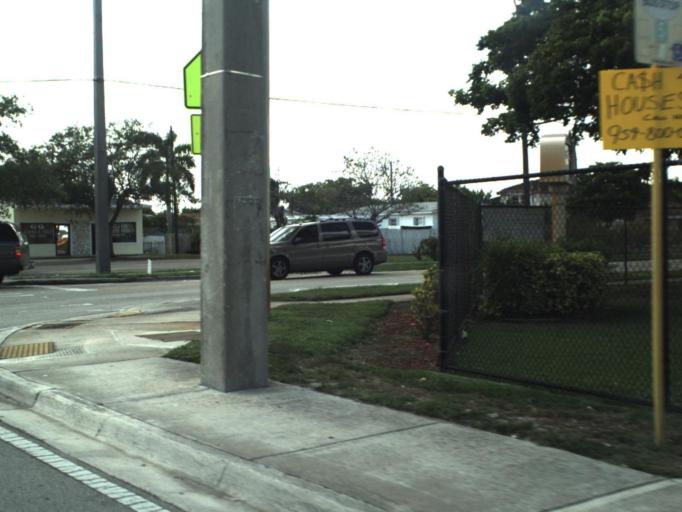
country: US
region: Florida
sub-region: Broward County
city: Carver Ranches
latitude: 25.9954
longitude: -80.1949
